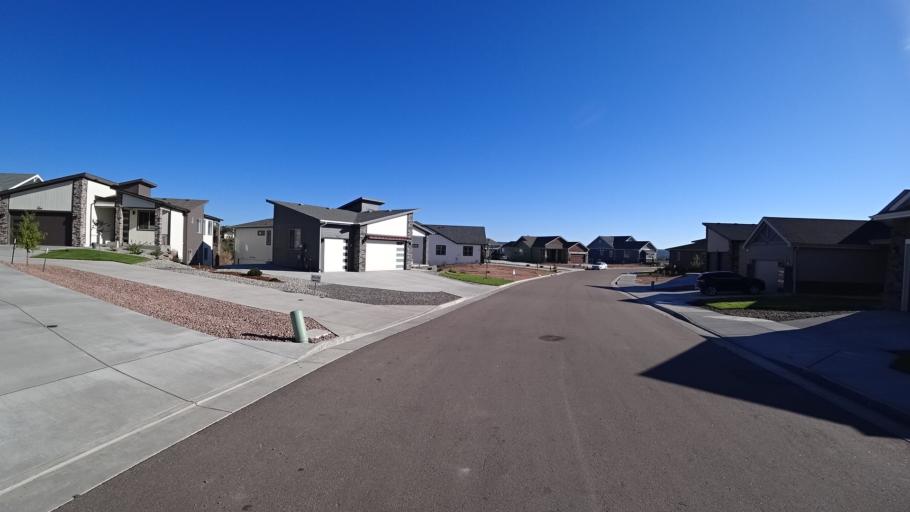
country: US
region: Colorado
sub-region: El Paso County
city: Colorado Springs
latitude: 38.8457
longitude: -104.8376
